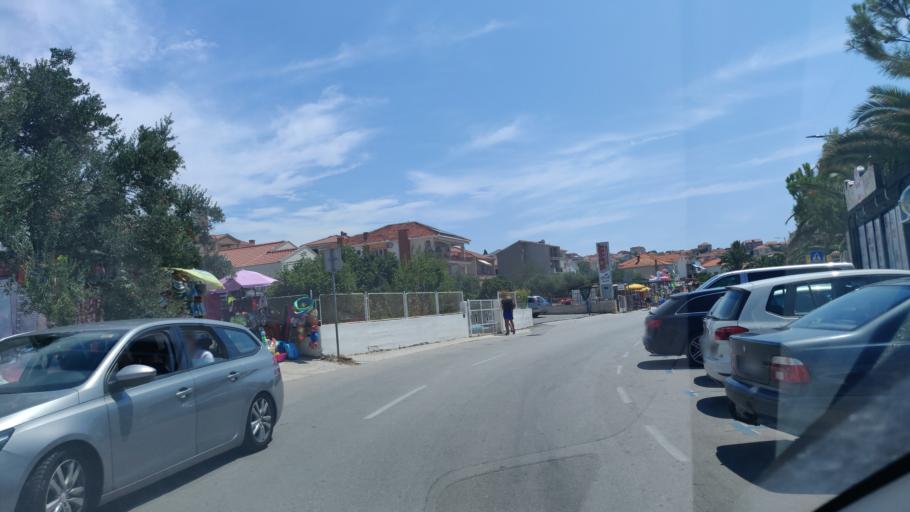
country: HR
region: Splitsko-Dalmatinska
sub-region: Grad Trogir
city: Trogir
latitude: 43.4993
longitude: 16.2600
